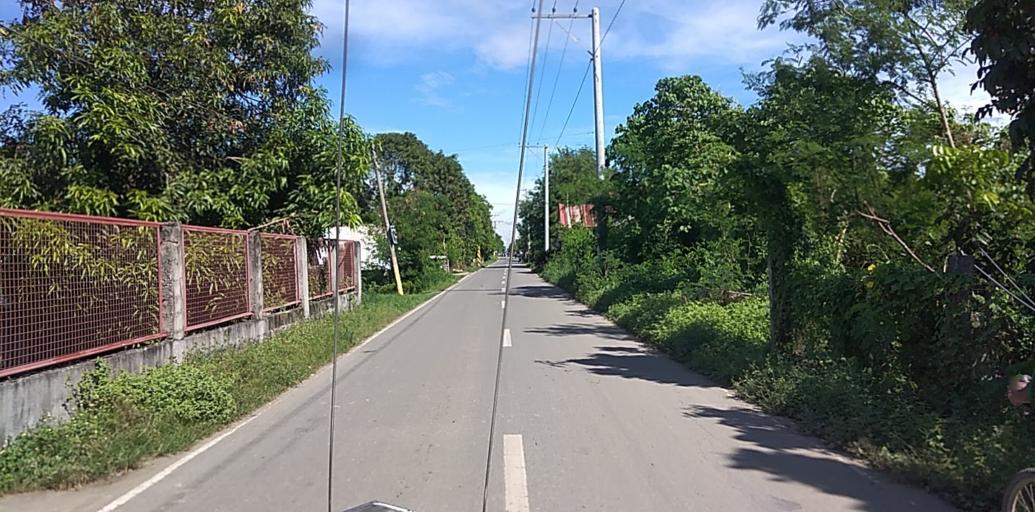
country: PH
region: Central Luzon
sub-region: Province of Pampanga
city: Candaba
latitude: 15.0817
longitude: 120.8091
